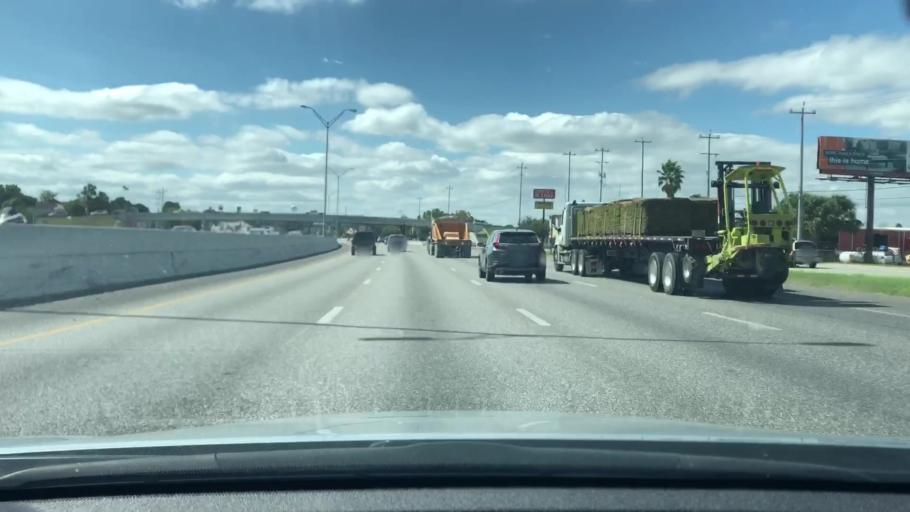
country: US
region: Texas
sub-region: Bexar County
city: Selma
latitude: 29.5792
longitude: -98.3191
